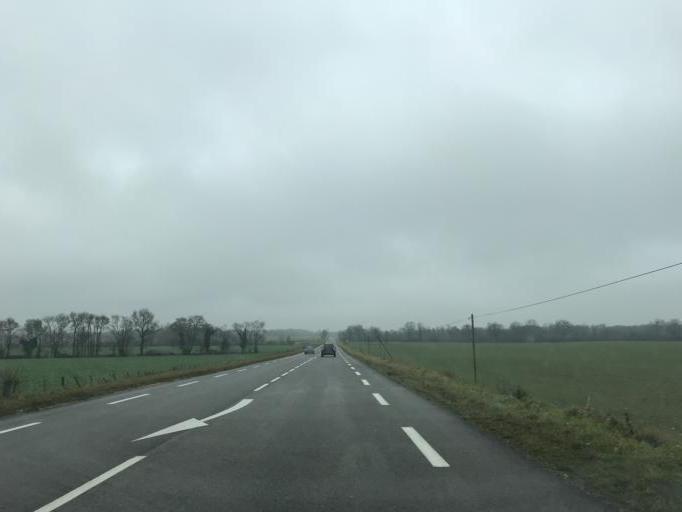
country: FR
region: Rhone-Alpes
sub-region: Departement de l'Ain
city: Villars-les-Dombes
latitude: 46.0256
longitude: 5.0586
